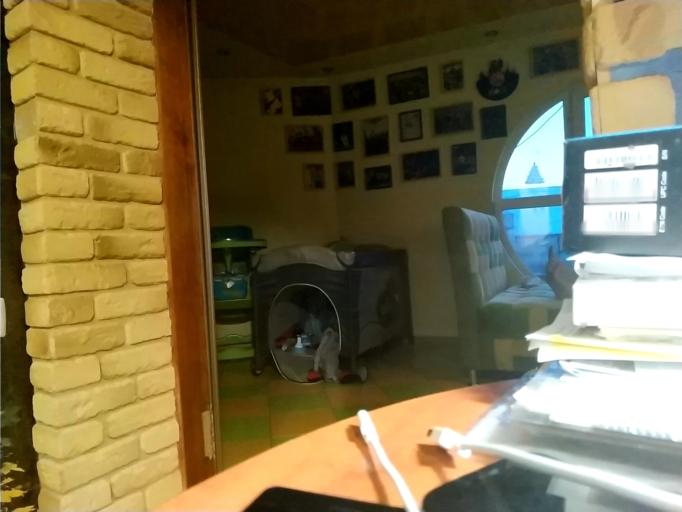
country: RU
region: Republic of Karelia
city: Belomorsk
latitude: 64.4527
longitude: 34.6140
